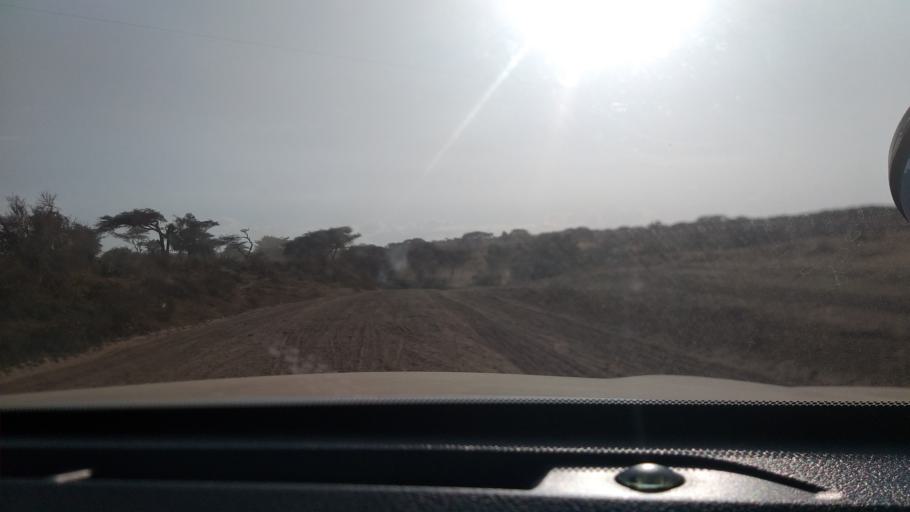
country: ET
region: Oromiya
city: Shashemene
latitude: 7.4873
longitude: 38.7259
